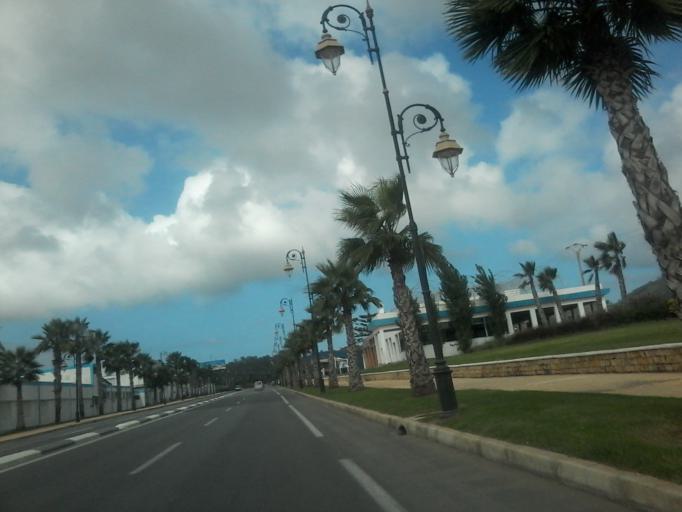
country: MA
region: Tanger-Tetouan
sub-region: Tetouan
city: Martil
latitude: 35.6560
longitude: -5.3191
